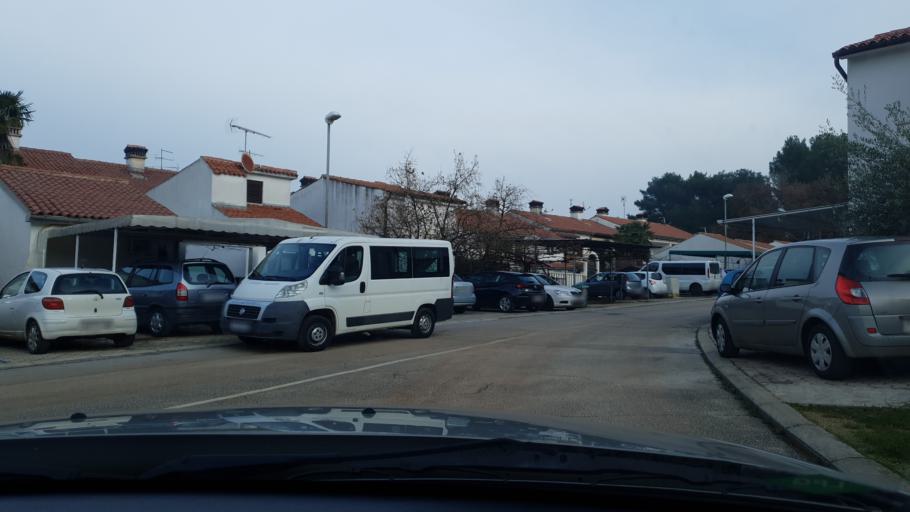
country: HR
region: Istarska
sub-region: Grad Porec
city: Porec
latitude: 45.2190
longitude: 13.6016
